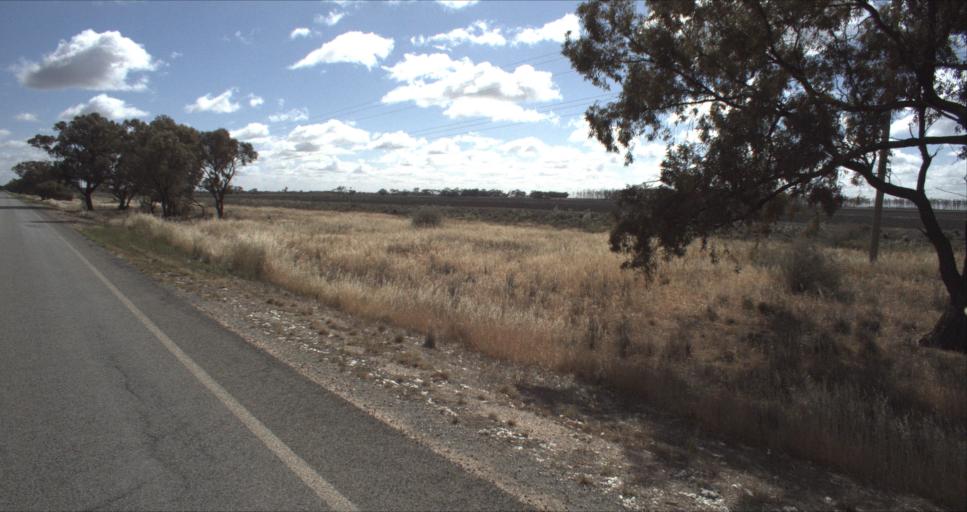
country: AU
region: New South Wales
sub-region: Murrumbidgee Shire
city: Darlington Point
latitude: -34.5642
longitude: 146.1685
